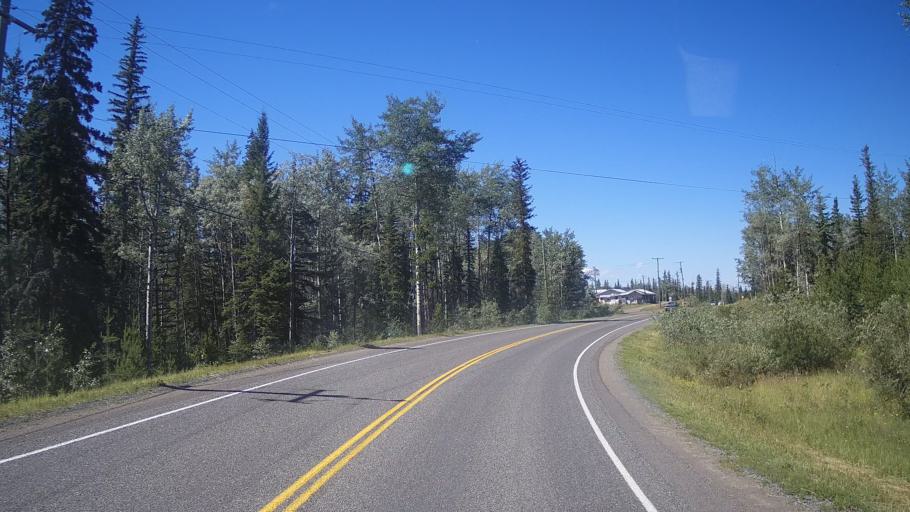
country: CA
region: British Columbia
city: Cache Creek
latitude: 51.5532
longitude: -121.2229
